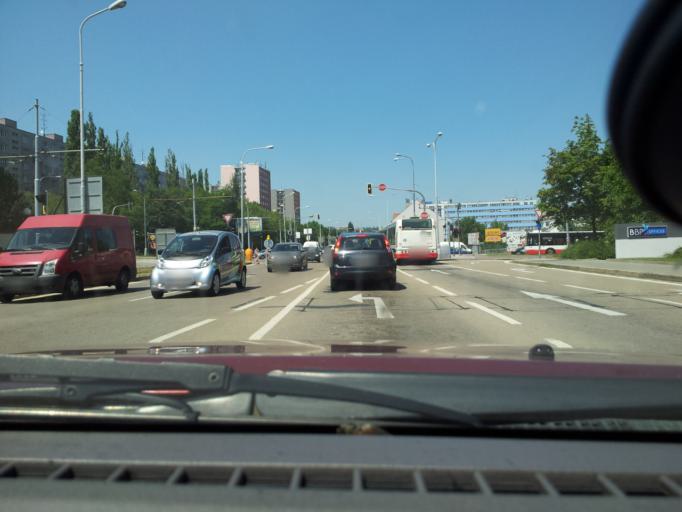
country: CZ
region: South Moravian
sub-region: Mesto Brno
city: Brno
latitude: 49.1720
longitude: 16.5974
